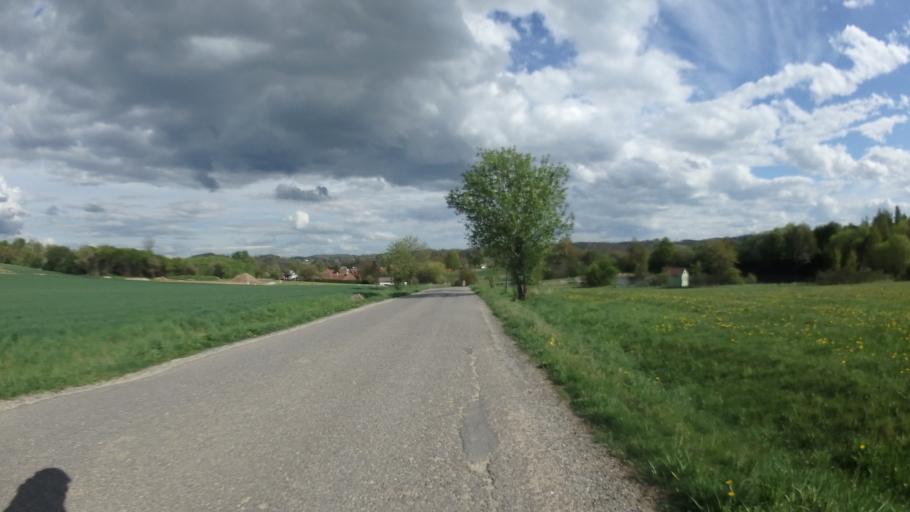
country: CZ
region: Vysocina
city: Merin
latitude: 49.3402
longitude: 15.8944
